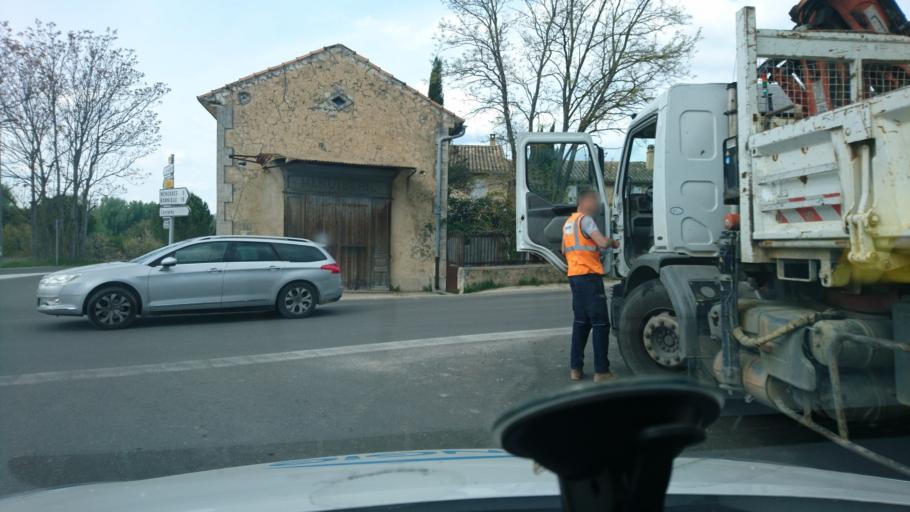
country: FR
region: Provence-Alpes-Cote d'Azur
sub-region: Departement du Vaucluse
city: Maubec
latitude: 43.8522
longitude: 5.1617
